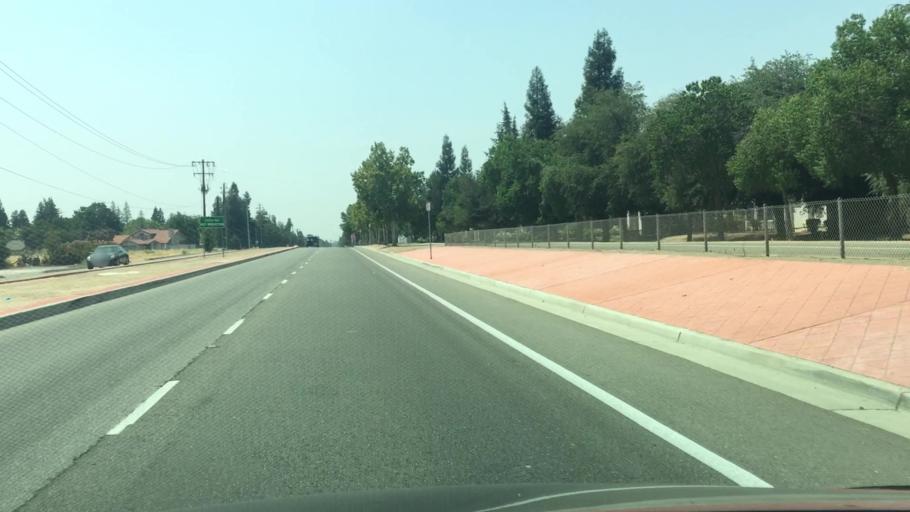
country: US
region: California
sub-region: Fresno County
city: Clovis
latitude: 36.8666
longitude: -119.7497
